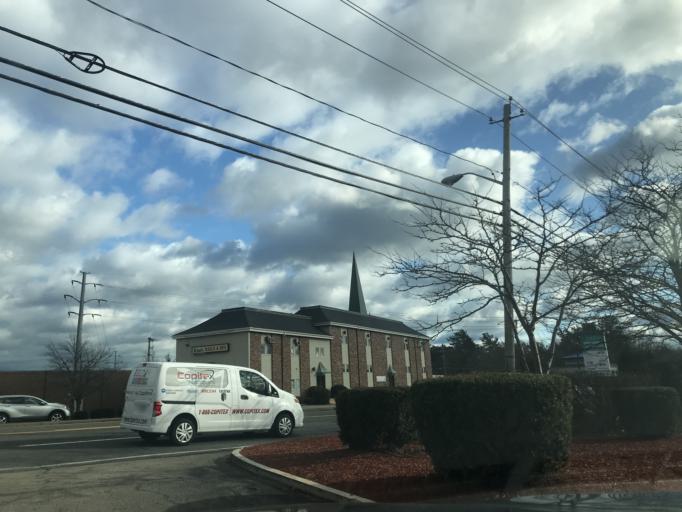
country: US
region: Massachusetts
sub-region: Plymouth County
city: Hanover
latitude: 42.1445
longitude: -70.8448
